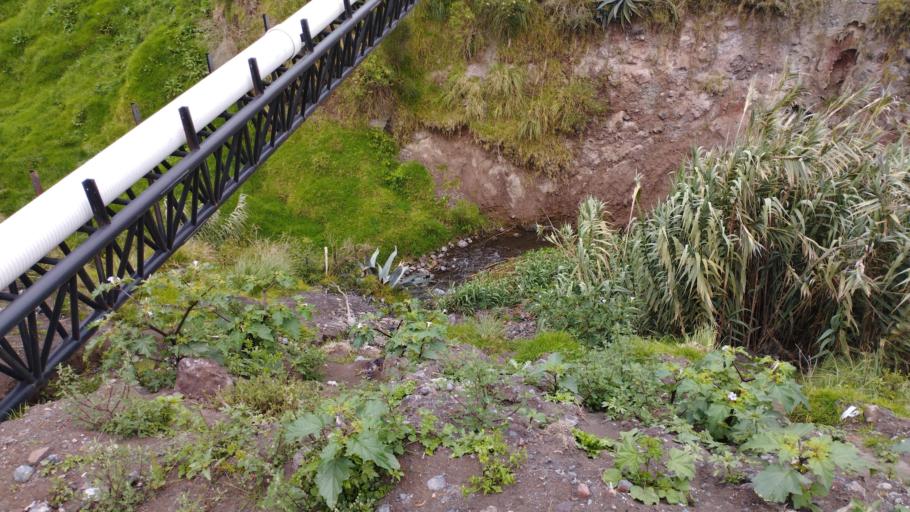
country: EC
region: Chimborazo
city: Guano
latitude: -1.6227
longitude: -78.6096
